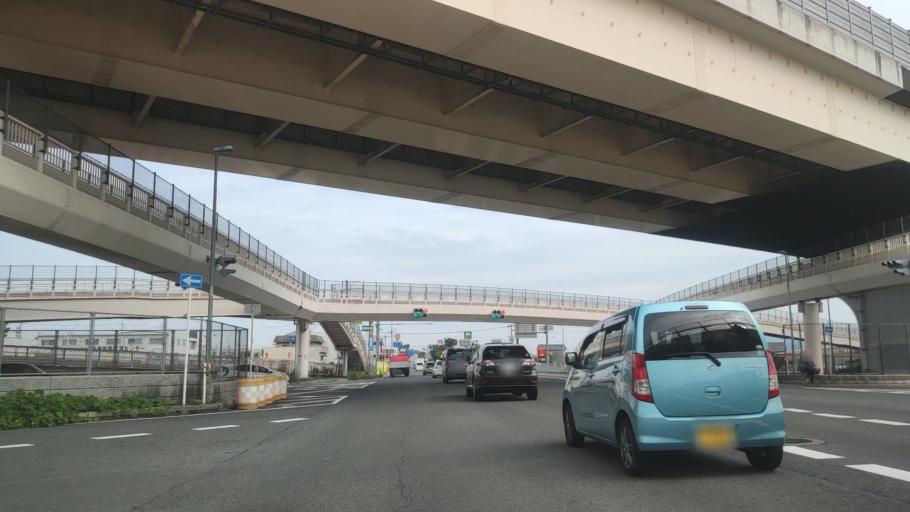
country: JP
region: Osaka
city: Tondabayashicho
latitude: 34.5336
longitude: 135.6047
